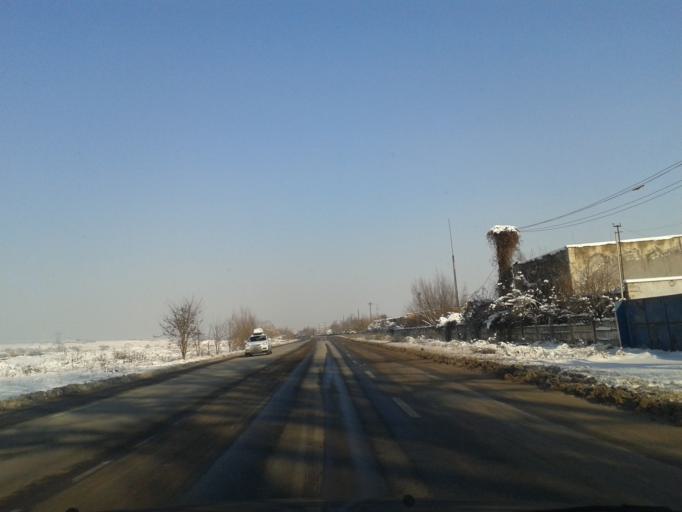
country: RO
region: Hunedoara
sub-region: Municipiul Hunedoara
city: Pestisu Mare
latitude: 45.8097
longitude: 22.9295
